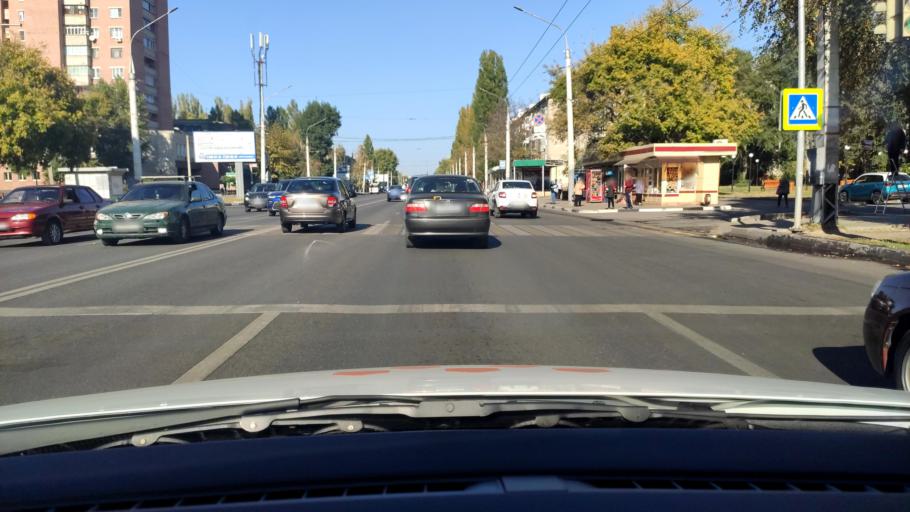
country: RU
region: Voronezj
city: Voronezh
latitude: 51.6520
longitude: 39.2421
